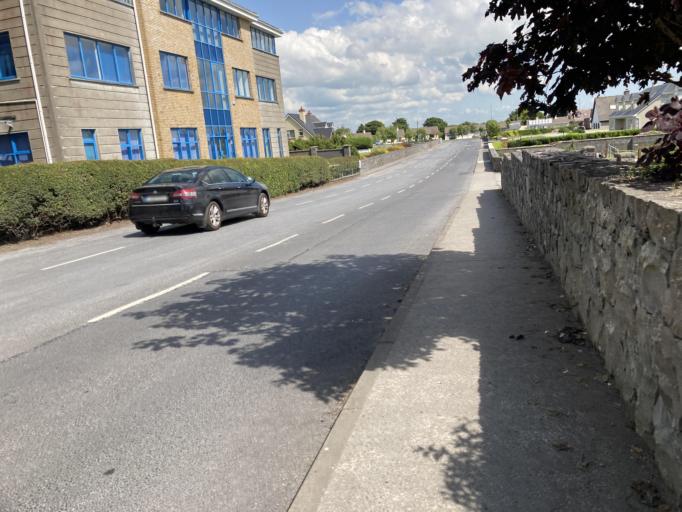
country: IE
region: Connaught
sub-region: County Galway
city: Claregalway
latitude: 53.2975
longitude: -8.9888
